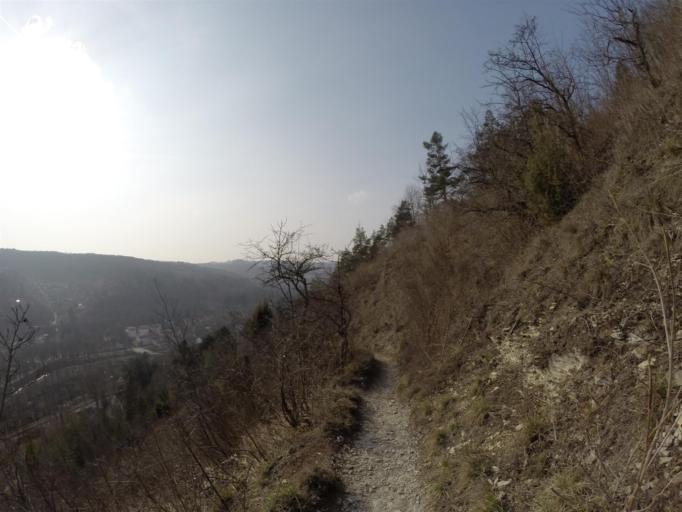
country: DE
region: Thuringia
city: Jena
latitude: 50.9374
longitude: 11.5621
